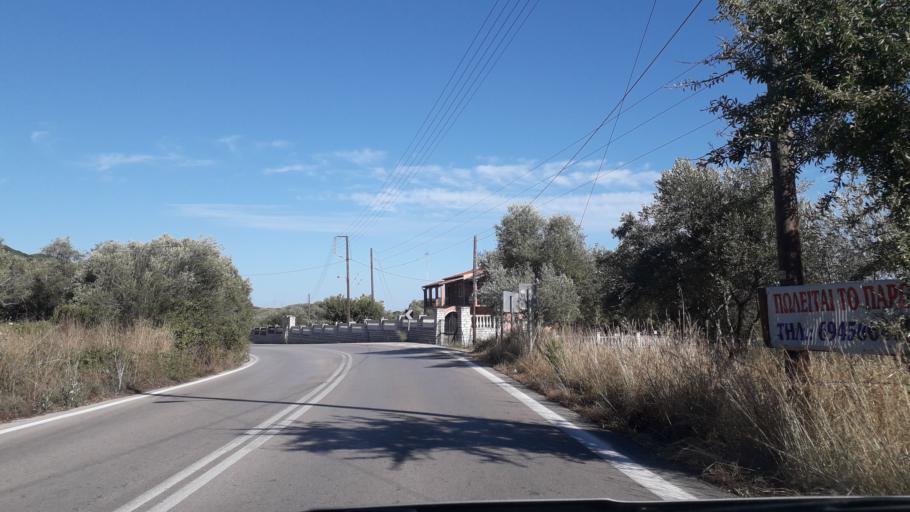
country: GR
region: Ionian Islands
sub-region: Nomos Kerkyras
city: Agios Matthaios
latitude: 39.4577
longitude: 19.9156
